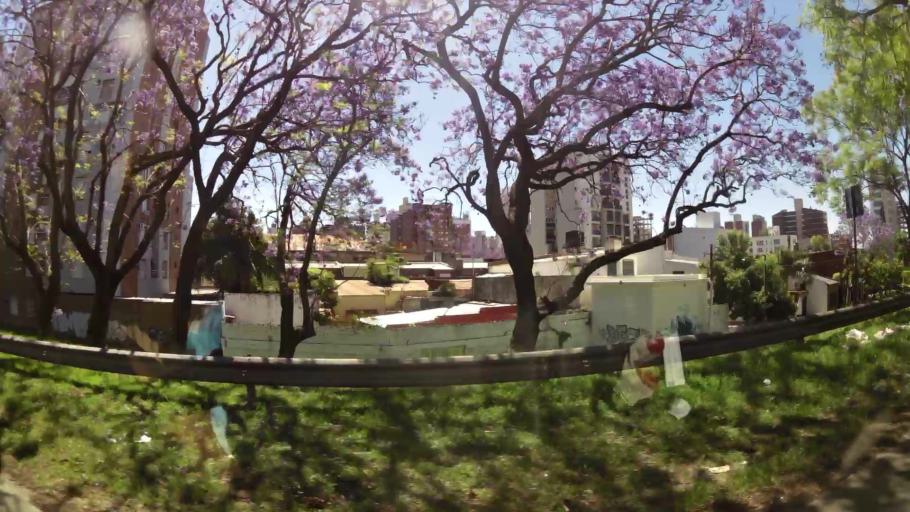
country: AR
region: Santa Fe
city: Santa Fe de la Vera Cruz
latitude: -31.6578
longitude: -60.7067
